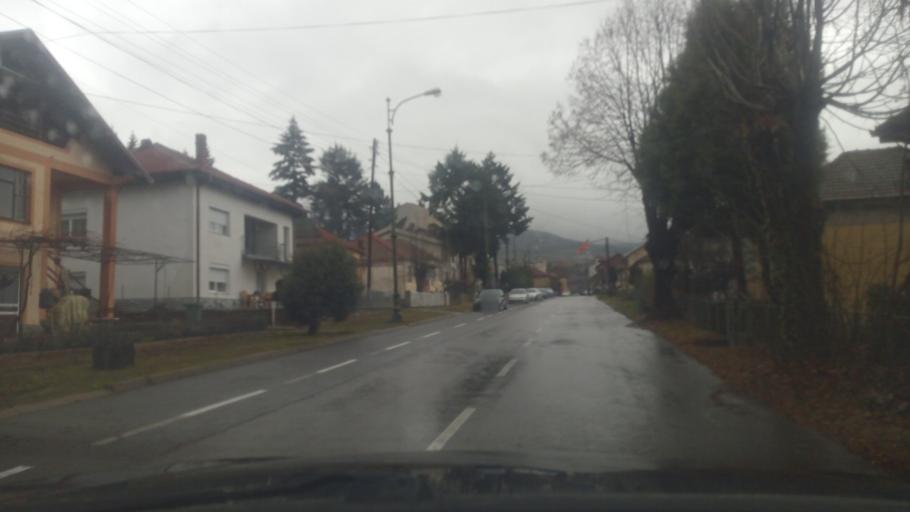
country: MK
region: Pehcevo
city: Pehcevo
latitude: 41.7616
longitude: 22.8833
